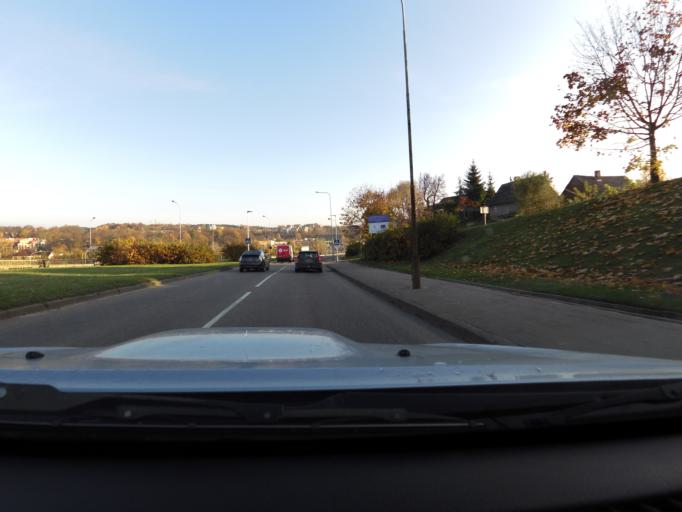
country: LT
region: Vilnius County
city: Rasos
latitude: 54.6752
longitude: 25.3066
